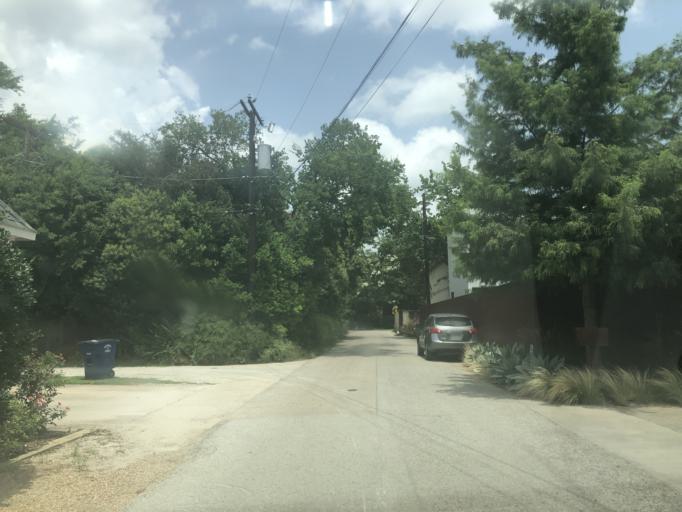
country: US
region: Texas
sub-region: Dallas County
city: University Park
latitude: 32.8555
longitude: -96.8228
